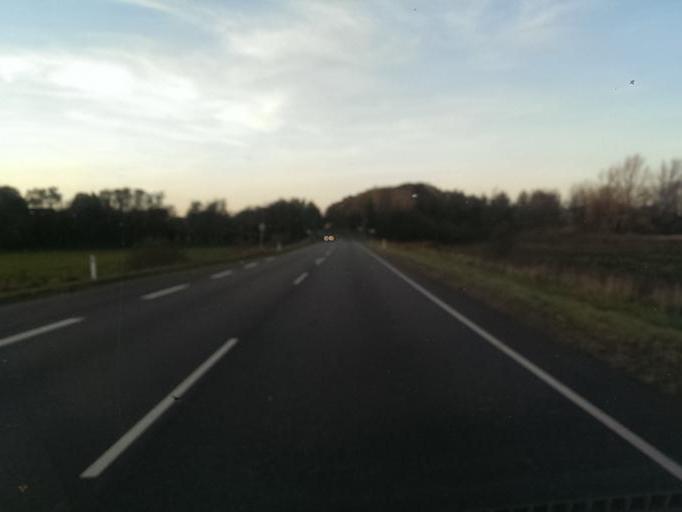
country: DK
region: South Denmark
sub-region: Esbjerg Kommune
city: Bramming
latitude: 55.4840
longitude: 8.6436
